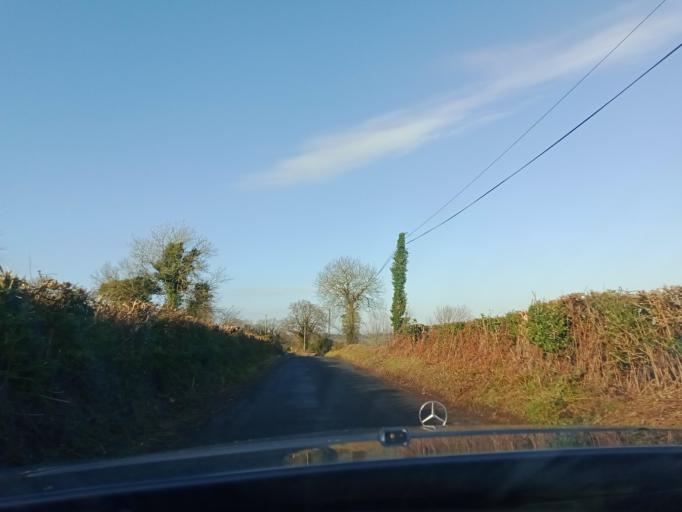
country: IE
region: Leinster
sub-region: Kilkenny
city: Callan
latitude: 52.4641
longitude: -7.3995
